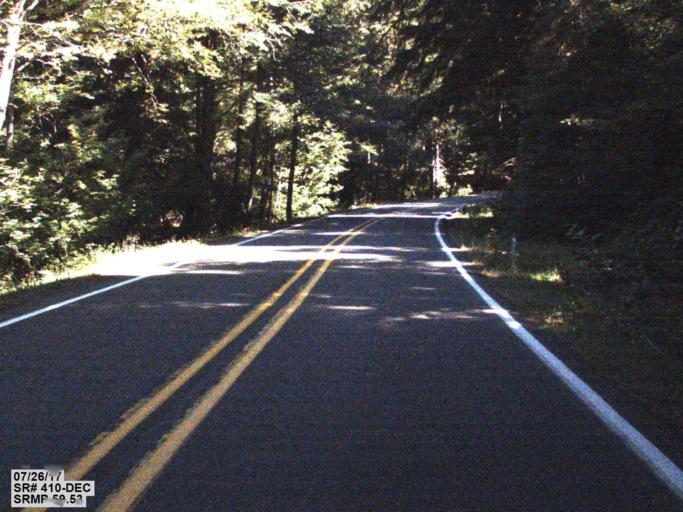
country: US
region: Washington
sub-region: King County
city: Enumclaw
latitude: 46.9530
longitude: -121.5301
